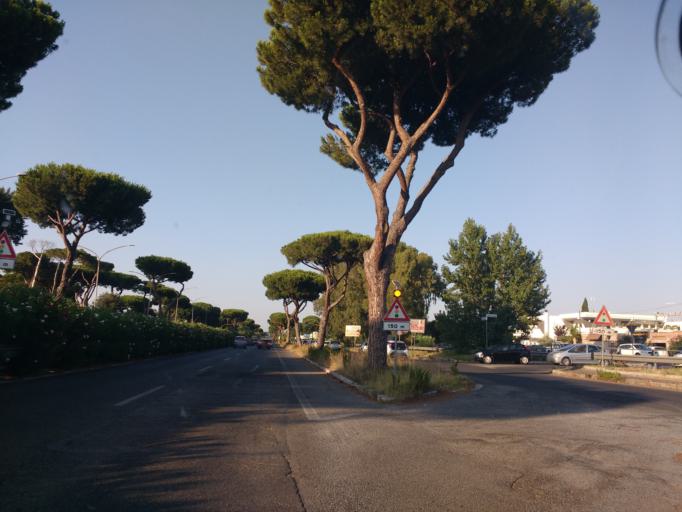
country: IT
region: Latium
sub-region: Citta metropolitana di Roma Capitale
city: Acilia-Castel Fusano-Ostia Antica
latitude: 41.7445
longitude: 12.3563
